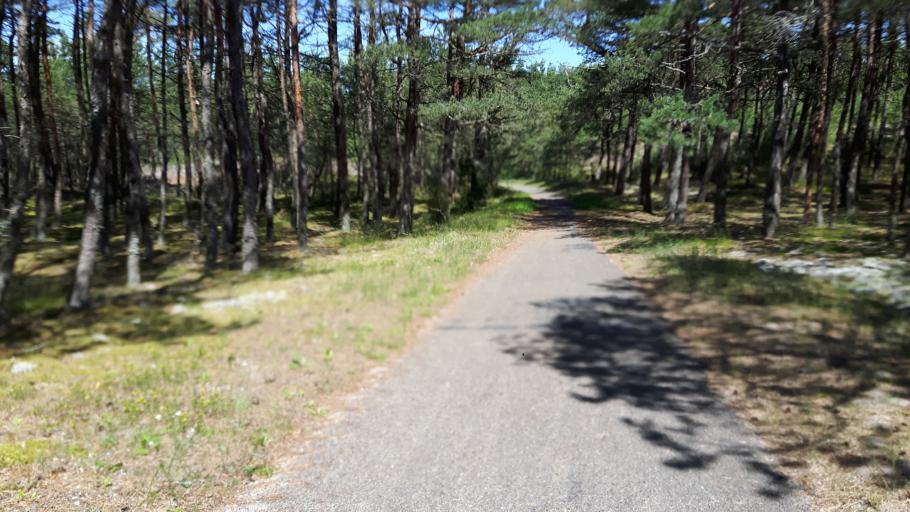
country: LT
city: Neringa
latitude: 55.4206
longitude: 21.0768
